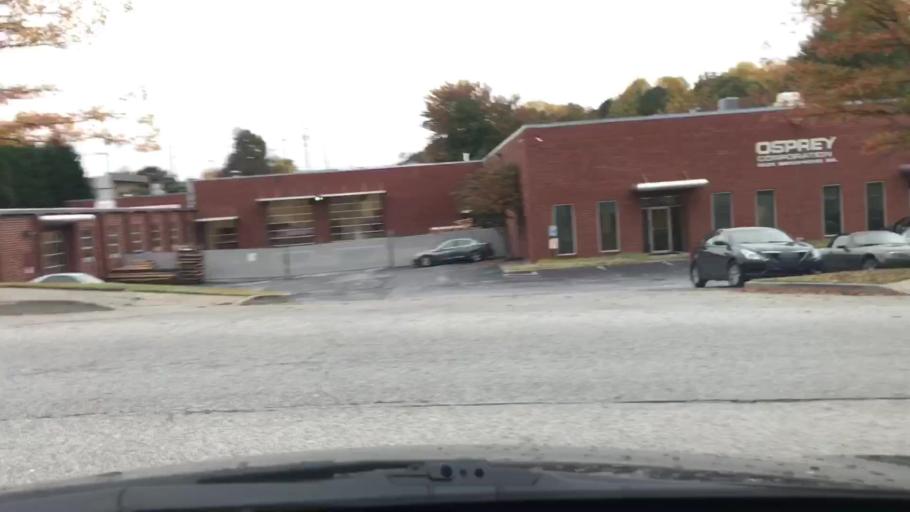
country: US
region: Georgia
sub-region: DeKalb County
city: North Druid Hills
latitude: 33.8409
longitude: -84.3215
